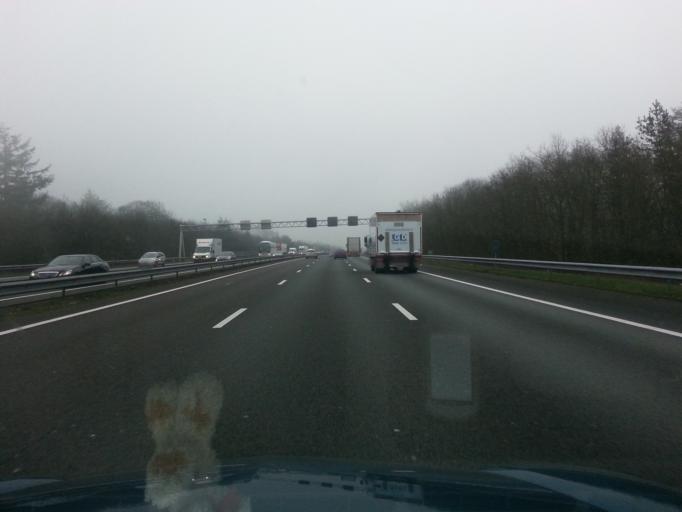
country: NL
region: Gelderland
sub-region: Gemeente Arnhem
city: Hoogkamp
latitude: 52.0267
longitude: 5.8687
